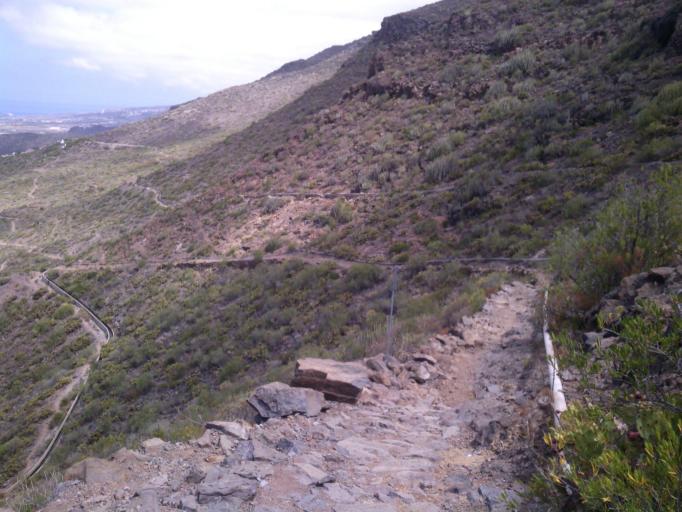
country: ES
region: Canary Islands
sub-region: Provincia de Santa Cruz de Tenerife
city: Arona
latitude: 28.0893
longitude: -16.6999
